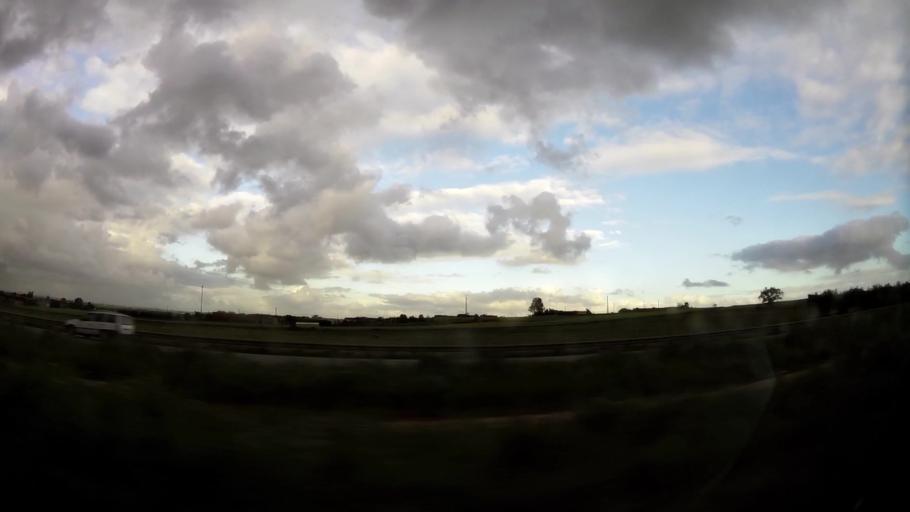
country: MA
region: Grand Casablanca
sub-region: Mediouna
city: Tit Mellil
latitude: 33.5809
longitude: -7.4527
